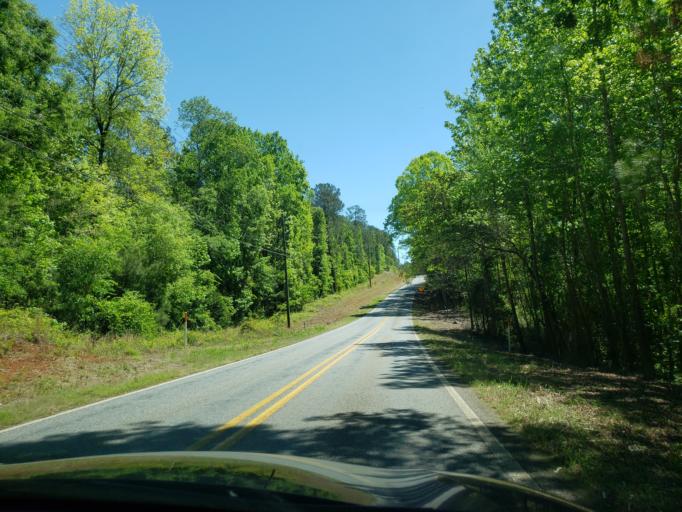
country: US
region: Alabama
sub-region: Tallapoosa County
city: Dadeville
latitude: 32.7072
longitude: -85.8333
